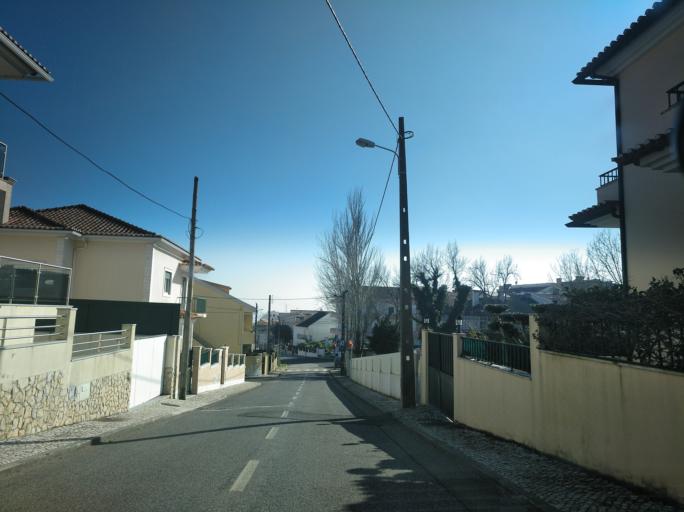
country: PT
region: Lisbon
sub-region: Odivelas
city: Famoes
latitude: 38.7981
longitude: -9.2176
